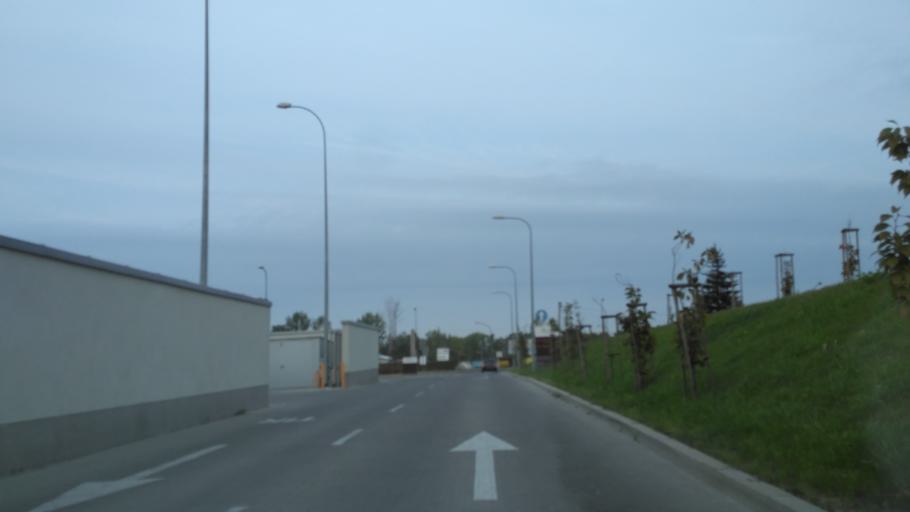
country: PL
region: Lublin Voivodeship
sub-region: Powiat lubelski
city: Jakubowice Murowane
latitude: 51.2311
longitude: 22.6180
